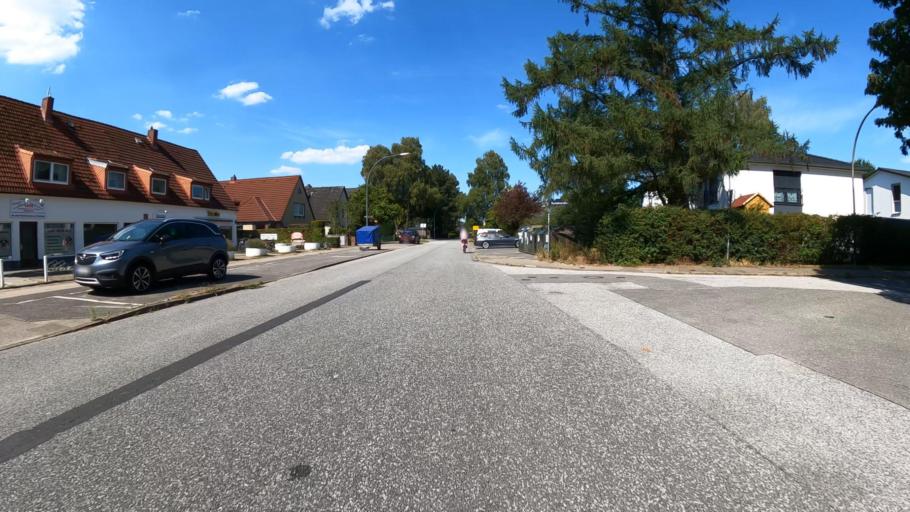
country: DE
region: Schleswig-Holstein
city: Halstenbek
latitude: 53.6161
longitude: 9.8749
